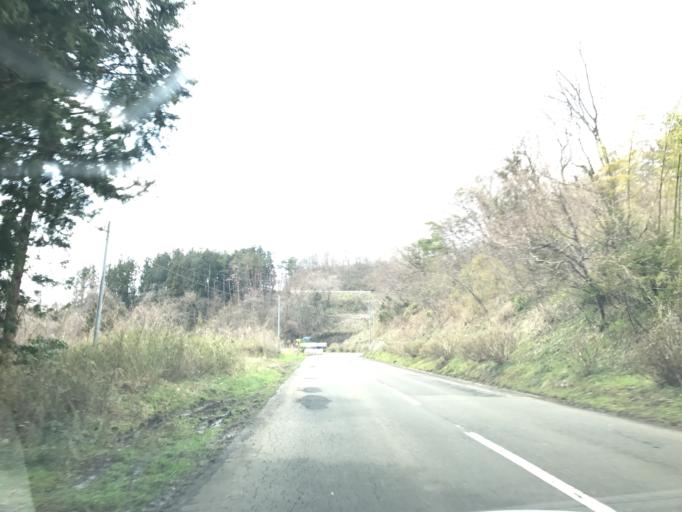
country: JP
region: Miyagi
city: Shiroishi
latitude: 38.0197
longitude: 140.5761
